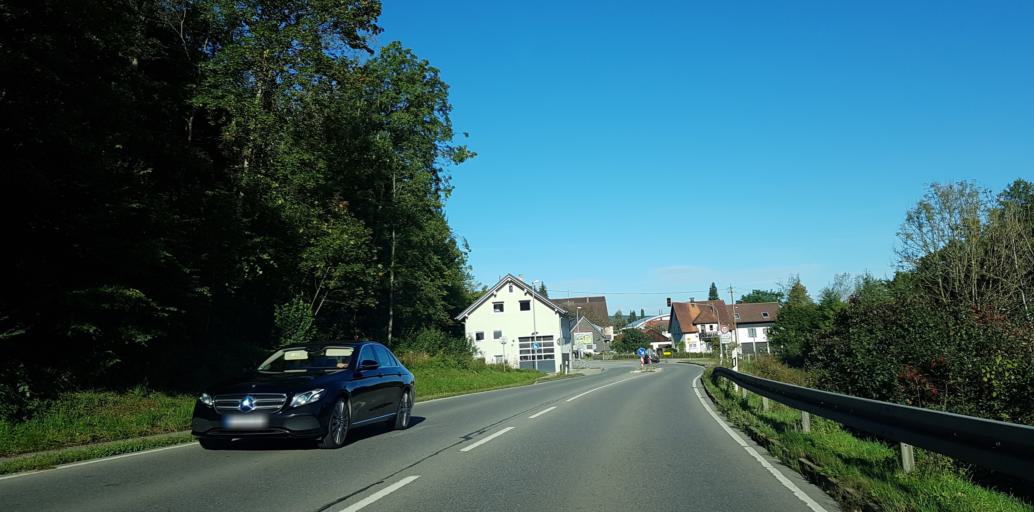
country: DE
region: Baden-Wuerttemberg
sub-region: Tuebingen Region
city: Leutkirch im Allgau
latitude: 47.8428
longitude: 9.9464
